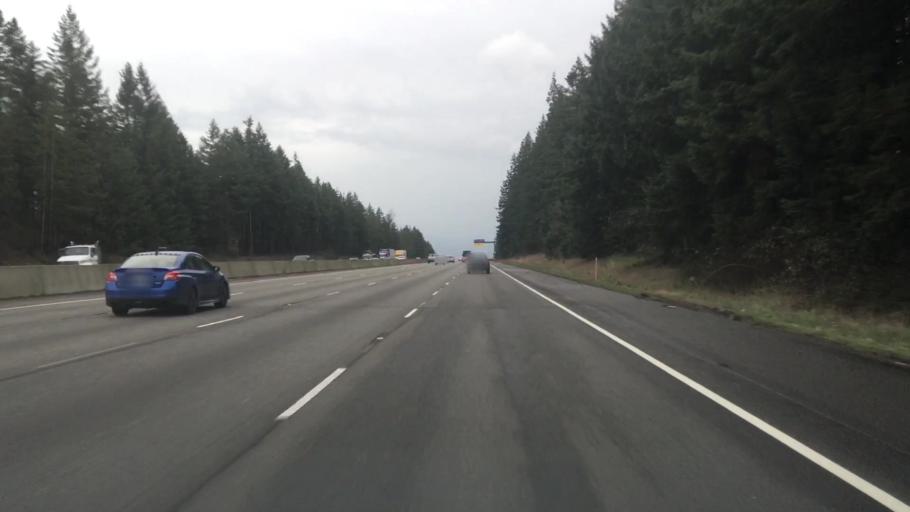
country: US
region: Washington
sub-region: Thurston County
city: Grand Mound
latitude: 46.8848
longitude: -122.9648
